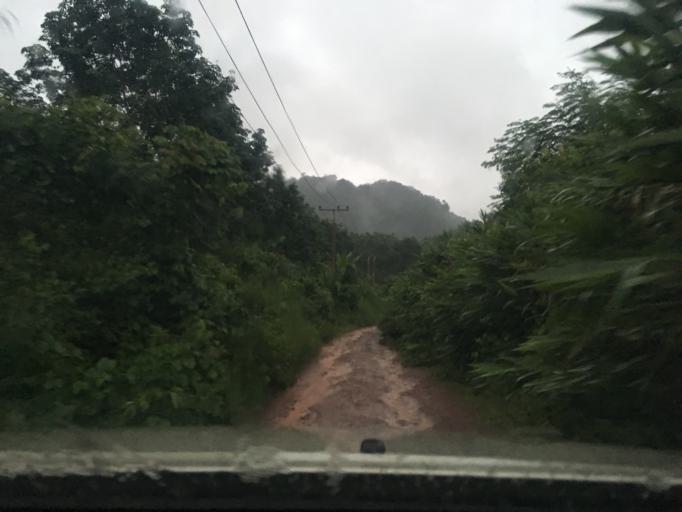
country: LA
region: Oudomxai
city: Muang La
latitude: 21.2436
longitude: 101.9382
